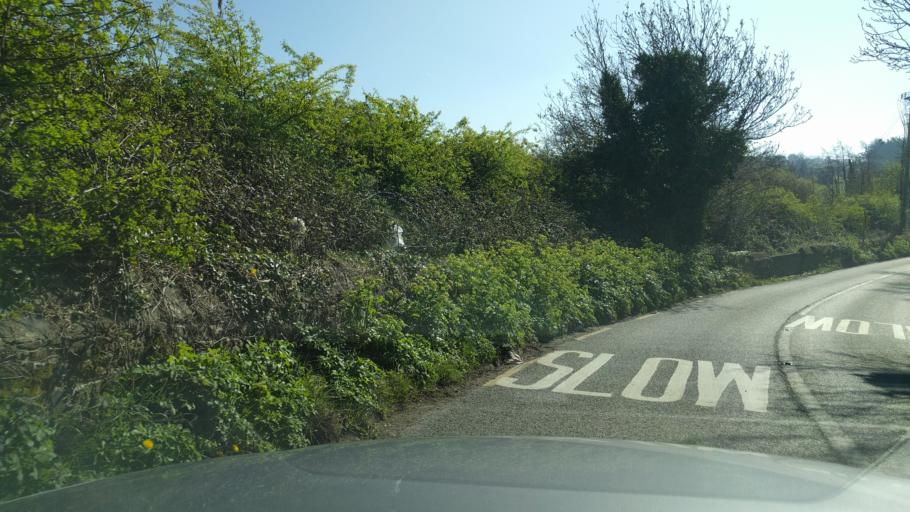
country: IE
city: Knocklyon
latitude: 53.2681
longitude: -6.3287
